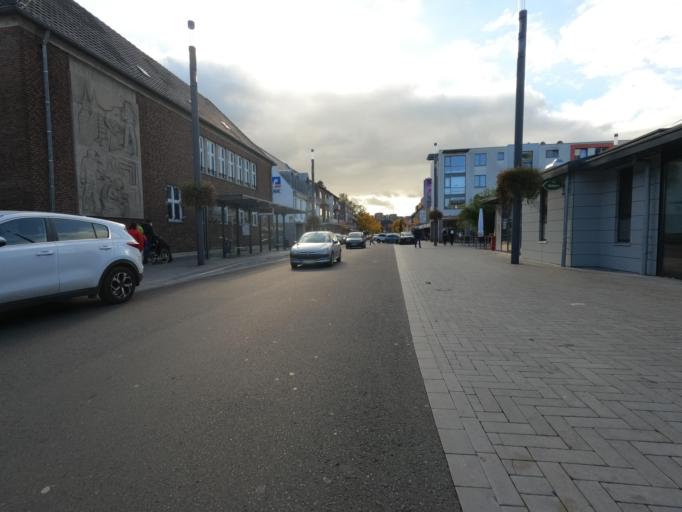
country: DE
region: North Rhine-Westphalia
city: Huckelhoven
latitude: 51.0550
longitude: 6.2235
